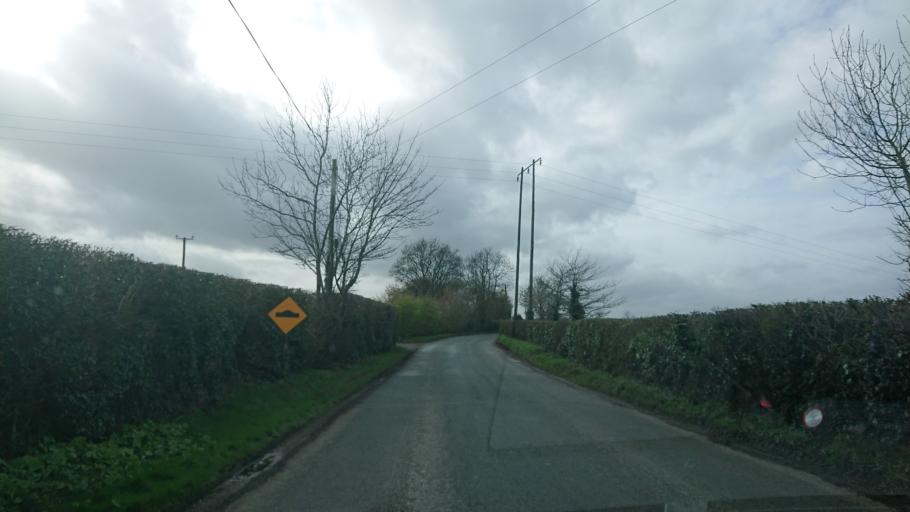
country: IE
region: Leinster
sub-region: Kildare
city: Naas
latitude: 53.1828
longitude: -6.6555
